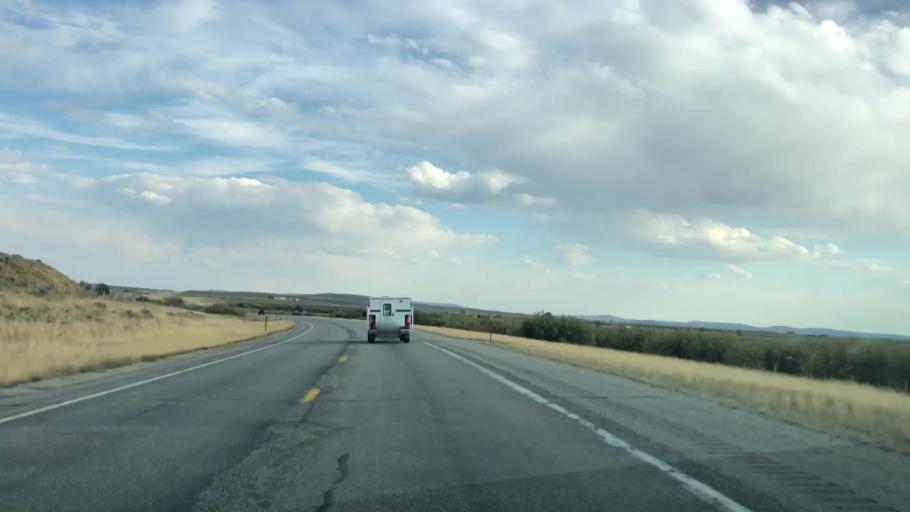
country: US
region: Wyoming
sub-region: Sublette County
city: Pinedale
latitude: 43.0224
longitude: -110.1227
